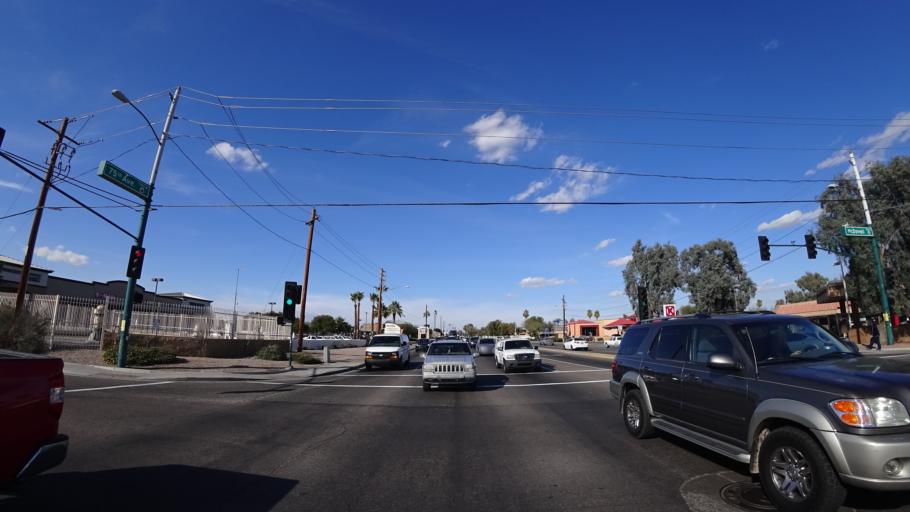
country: US
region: Arizona
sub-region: Maricopa County
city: Tolleson
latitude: 33.4658
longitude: -112.2206
